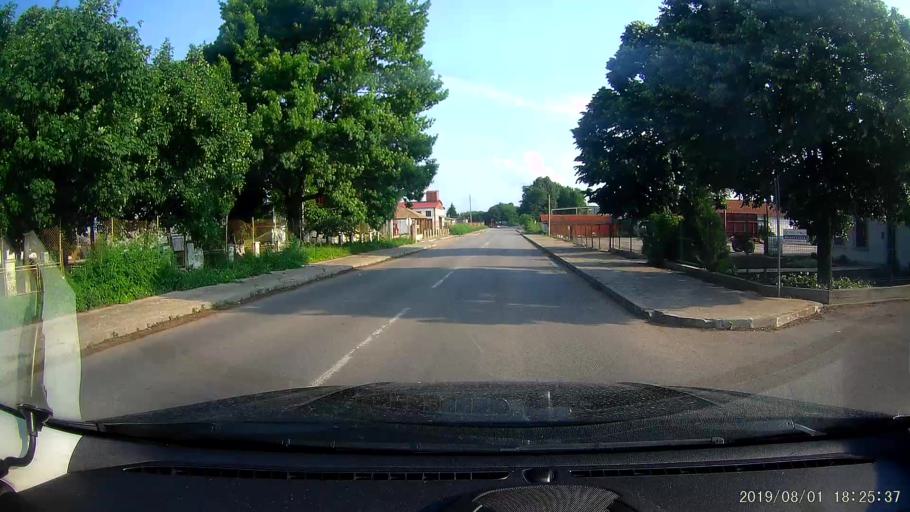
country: BG
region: Shumen
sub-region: Obshtina Venets
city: Venets
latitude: 43.6149
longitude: 26.9955
